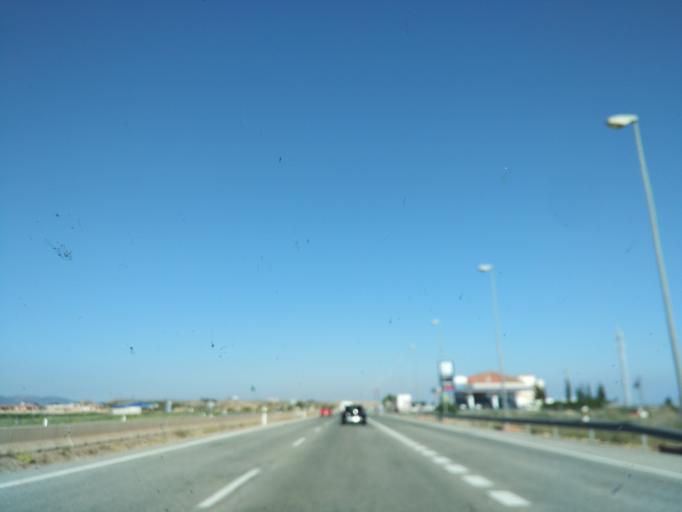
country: ES
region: Murcia
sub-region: Murcia
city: Murcia
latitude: 37.8672
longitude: -1.1101
